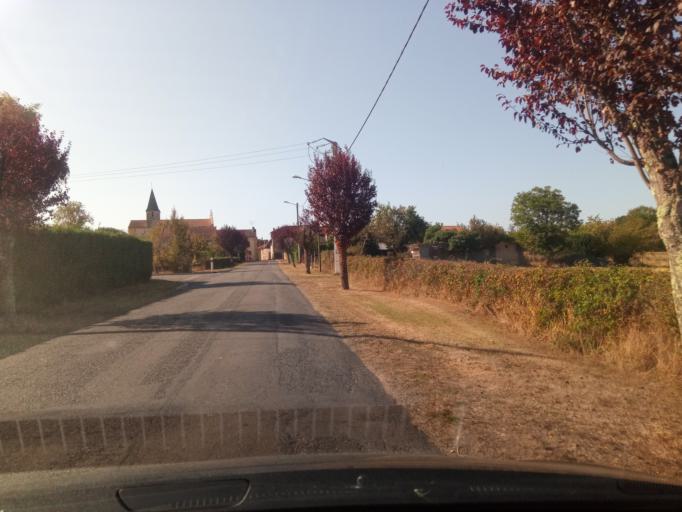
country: FR
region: Poitou-Charentes
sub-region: Departement de la Vienne
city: Saulge
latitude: 46.3347
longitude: 0.8735
